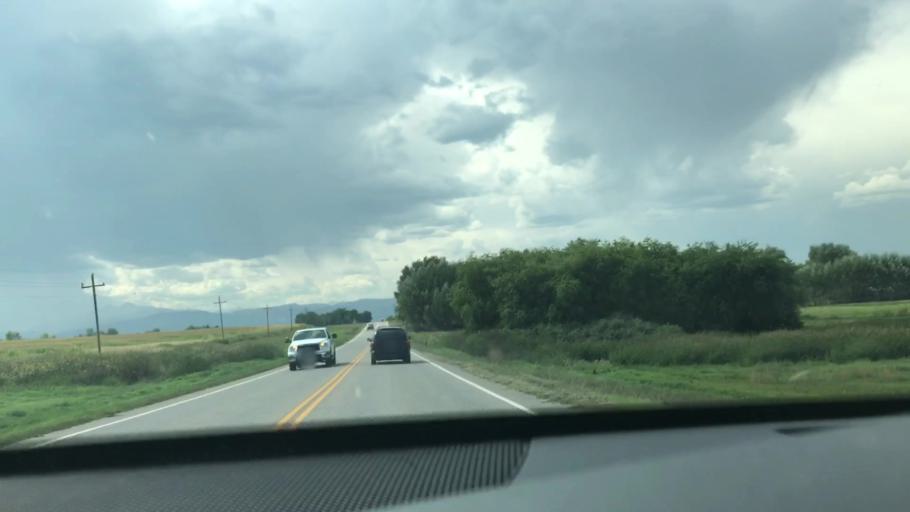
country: US
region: Colorado
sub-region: Larimer County
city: Loveland
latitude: 40.3795
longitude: -105.0044
